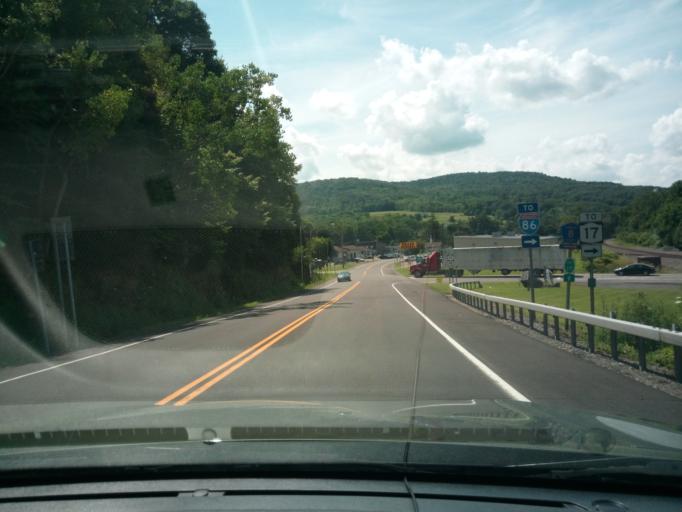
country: US
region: New York
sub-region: Chemung County
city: Southport
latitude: 42.0165
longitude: -76.7242
